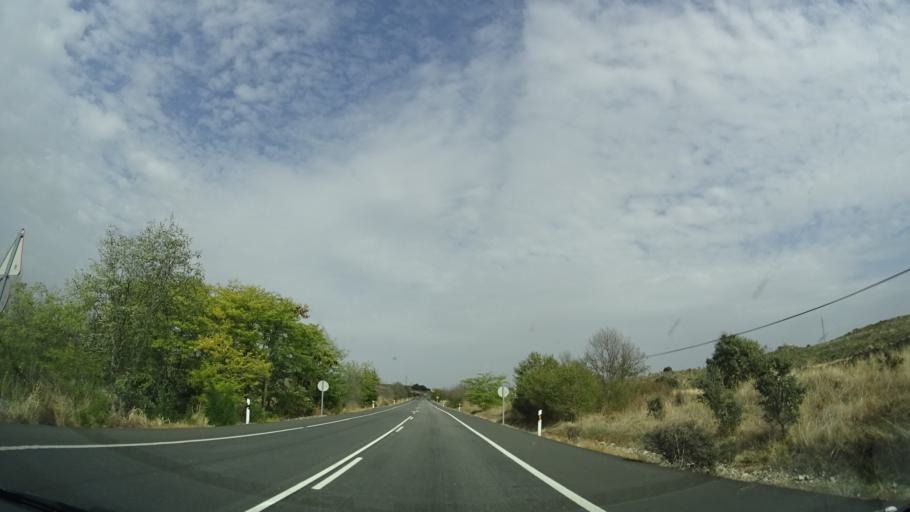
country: ES
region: Extremadura
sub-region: Provincia de Caceres
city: Trujillo
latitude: 39.4353
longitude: -5.8908
